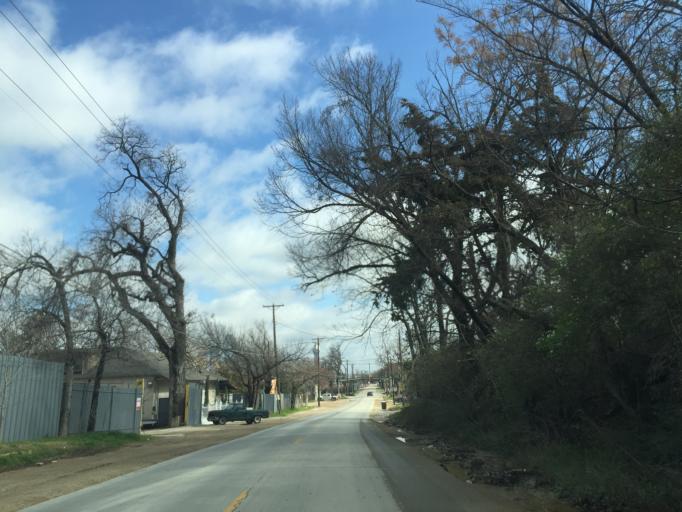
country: US
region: Texas
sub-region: Dallas County
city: Dallas
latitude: 32.7730
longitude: -96.8386
